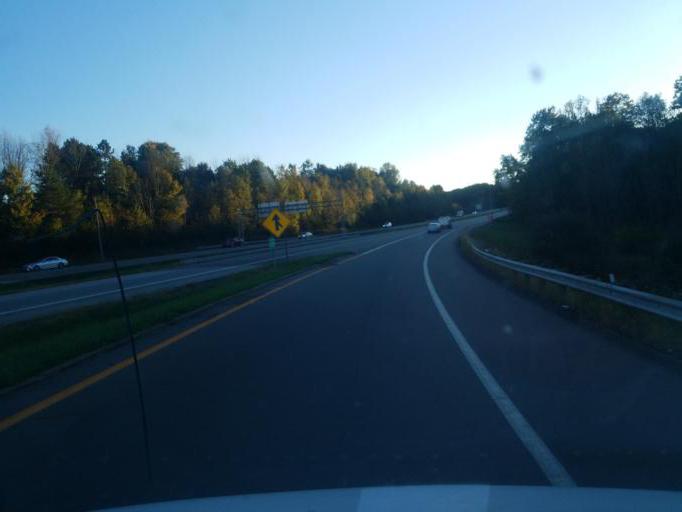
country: US
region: Ohio
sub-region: Stark County
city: Alliance
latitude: 40.9011
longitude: -81.1719
